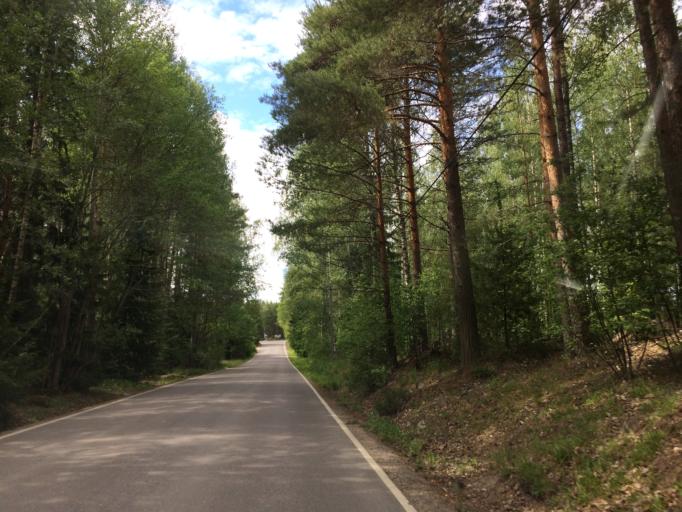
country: FI
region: Haeme
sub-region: Haemeenlinna
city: Janakkala
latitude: 60.8401
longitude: 24.5319
